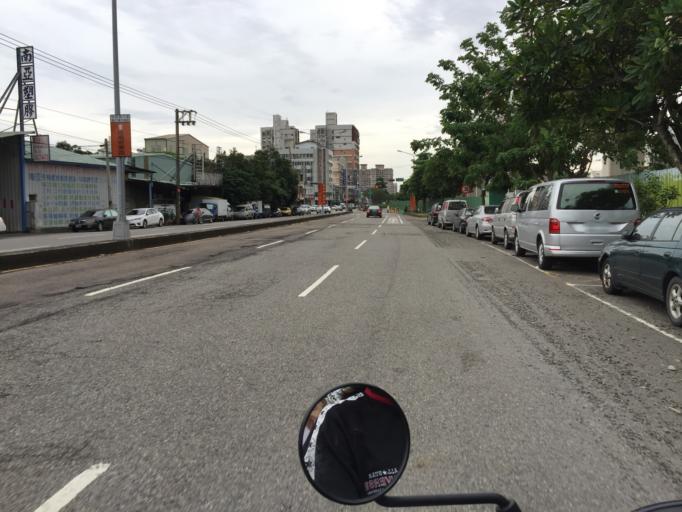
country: TW
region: Taiwan
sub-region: Taichung City
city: Taichung
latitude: 24.1618
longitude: 120.6996
